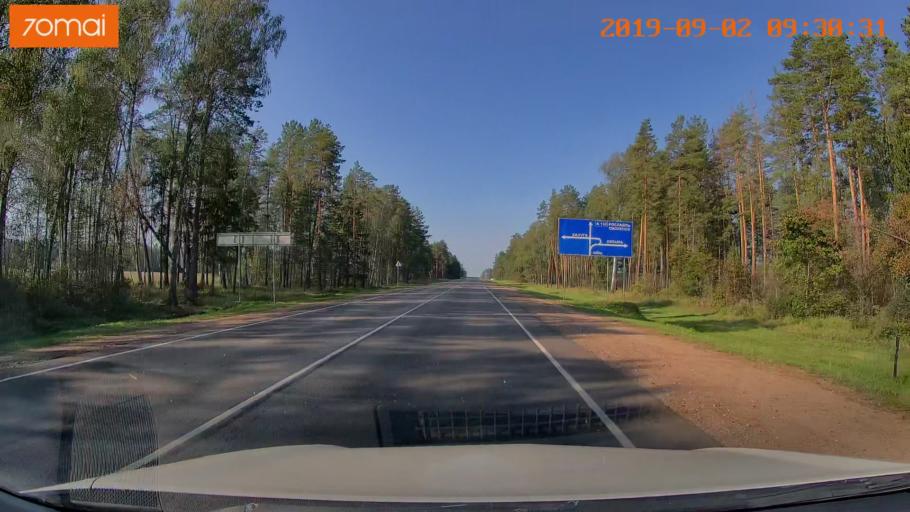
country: RU
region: Kaluga
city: Yukhnov
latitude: 54.7331
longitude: 35.1946
